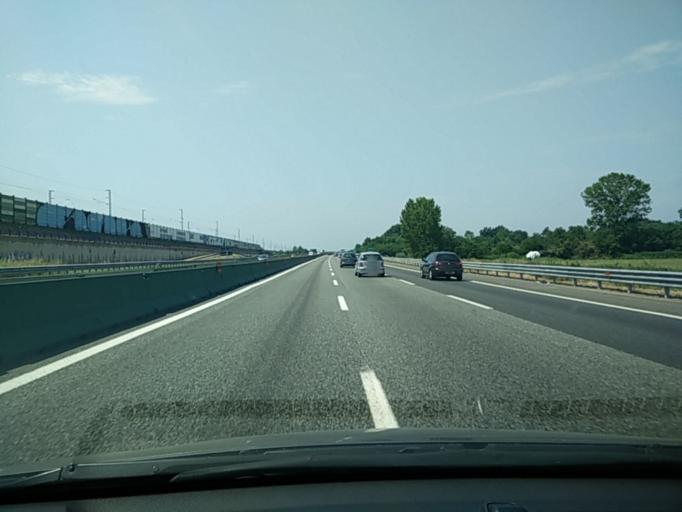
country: IT
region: Piedmont
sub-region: Provincia di Torino
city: Chivasso
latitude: 45.1996
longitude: 7.8668
